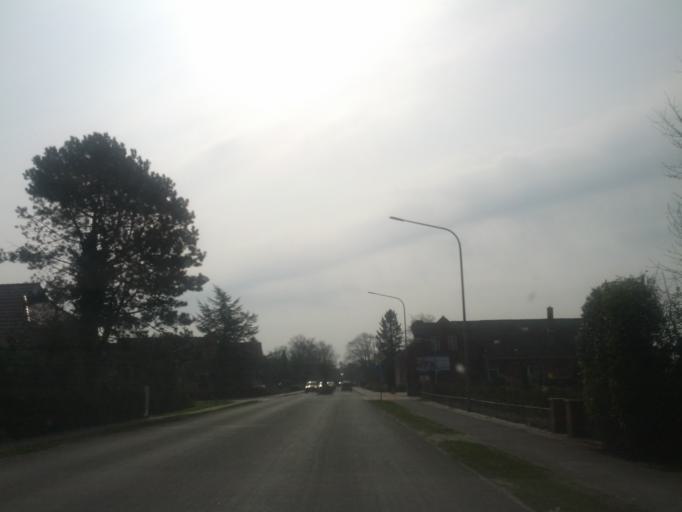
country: DE
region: Lower Saxony
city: Marienhafe
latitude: 53.5267
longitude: 7.2714
